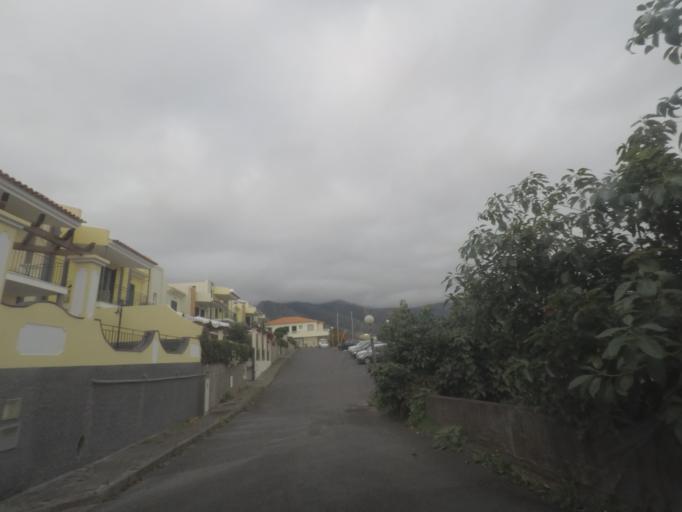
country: PT
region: Madeira
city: Camara de Lobos
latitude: 32.6622
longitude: -16.9455
